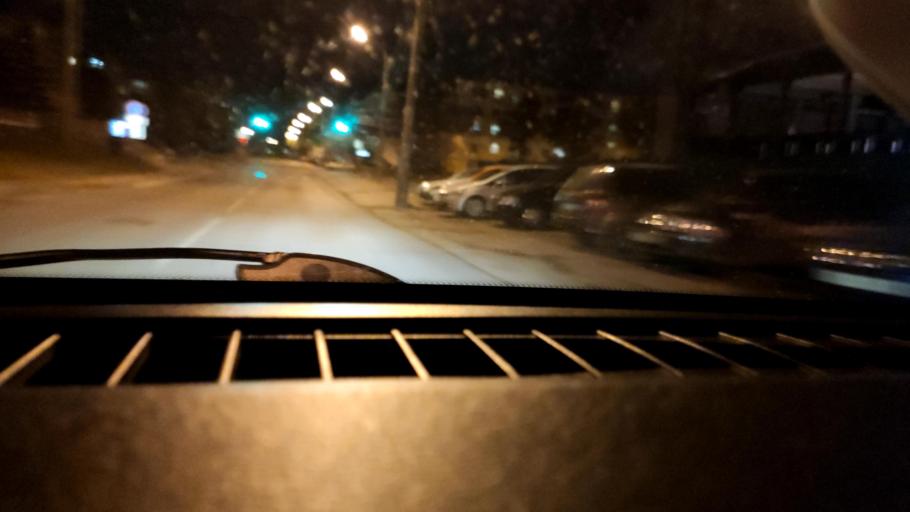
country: RU
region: Samara
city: Samara
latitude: 53.1944
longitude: 50.1717
